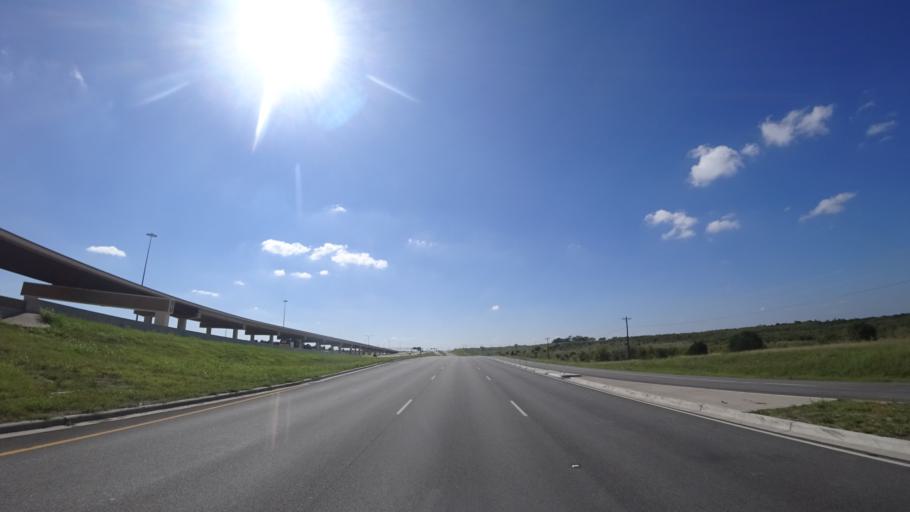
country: US
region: Texas
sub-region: Travis County
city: Manor
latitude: 30.3400
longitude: -97.5937
